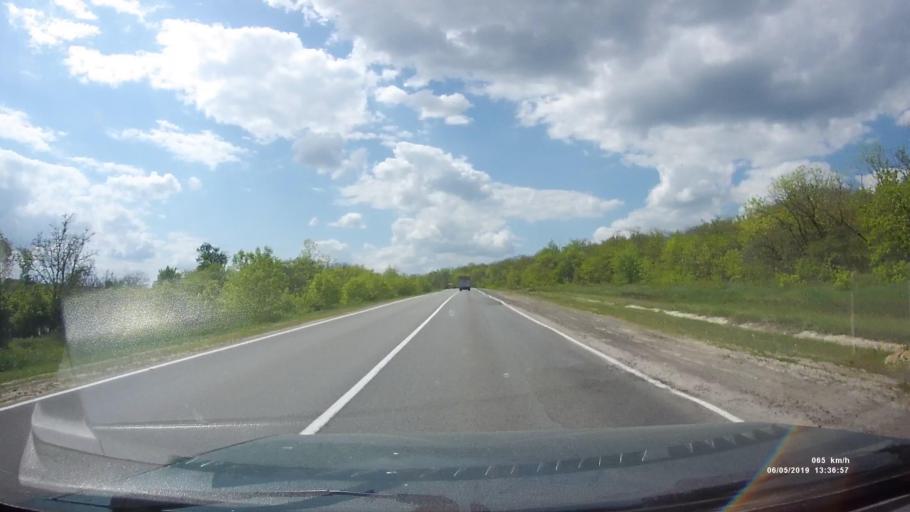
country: RU
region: Rostov
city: Ust'-Donetskiy
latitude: 47.6896
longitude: 40.7238
